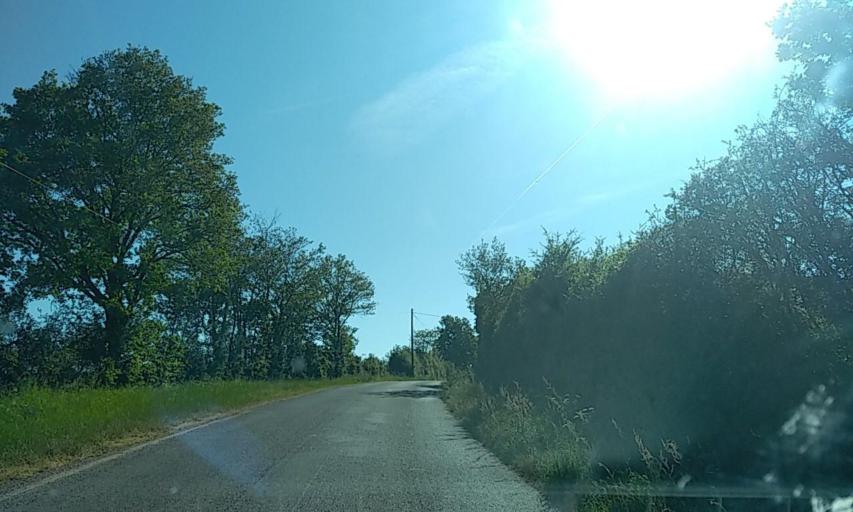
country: FR
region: Poitou-Charentes
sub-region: Departement des Deux-Sevres
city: Boisme
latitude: 46.8054
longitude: -0.4119
